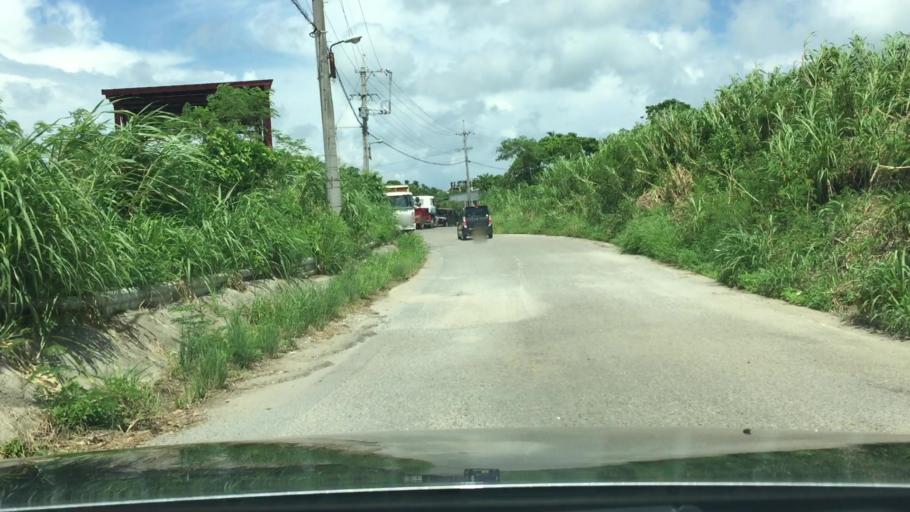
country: JP
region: Okinawa
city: Ishigaki
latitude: 24.3593
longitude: 124.1558
